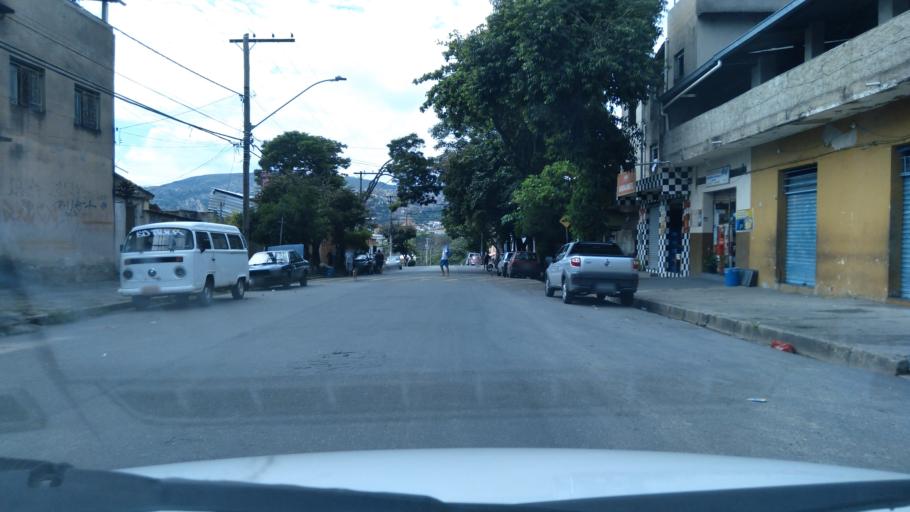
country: BR
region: Minas Gerais
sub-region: Belo Horizonte
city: Belo Horizonte
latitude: -19.8982
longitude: -43.8875
